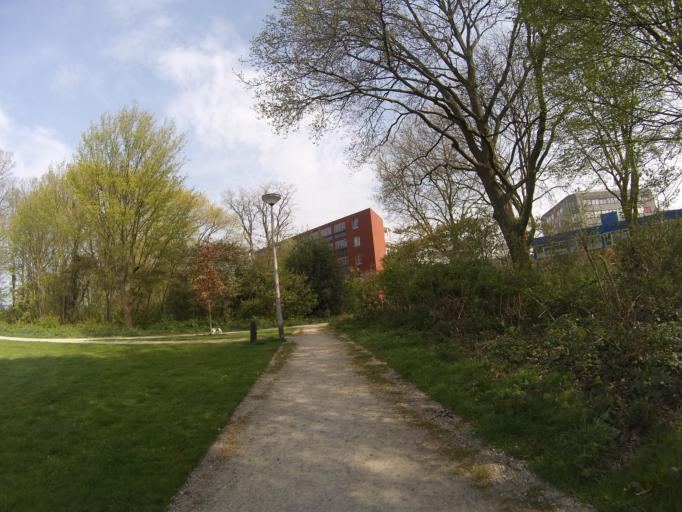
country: NL
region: Utrecht
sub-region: Gemeente Amersfoort
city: Amersfoort
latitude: 52.1601
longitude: 5.3737
